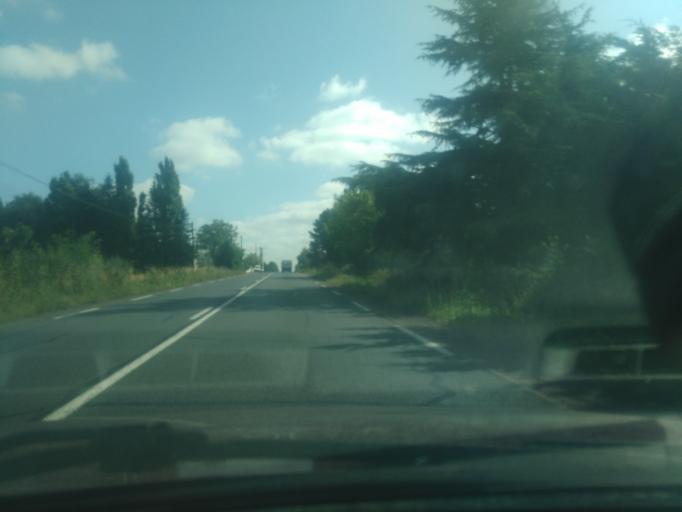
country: FR
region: Pays de la Loire
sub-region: Departement de la Vendee
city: Les Essarts
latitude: 46.7540
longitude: -1.2543
